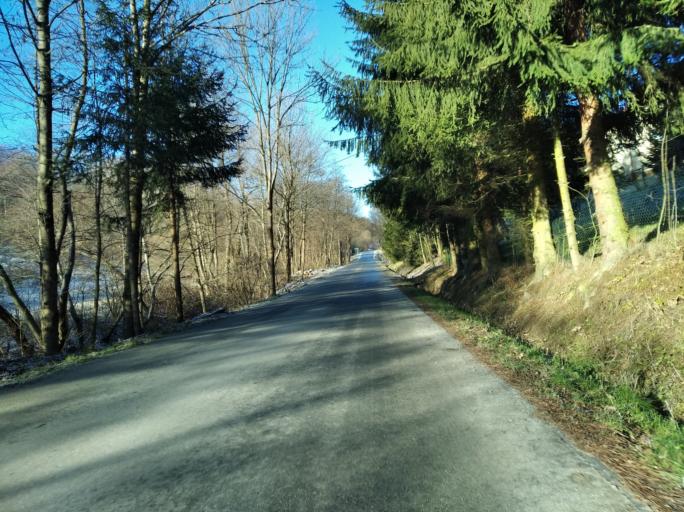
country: PL
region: Subcarpathian Voivodeship
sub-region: Powiat ropczycko-sedziszowski
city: Iwierzyce
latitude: 49.9577
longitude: 21.7631
